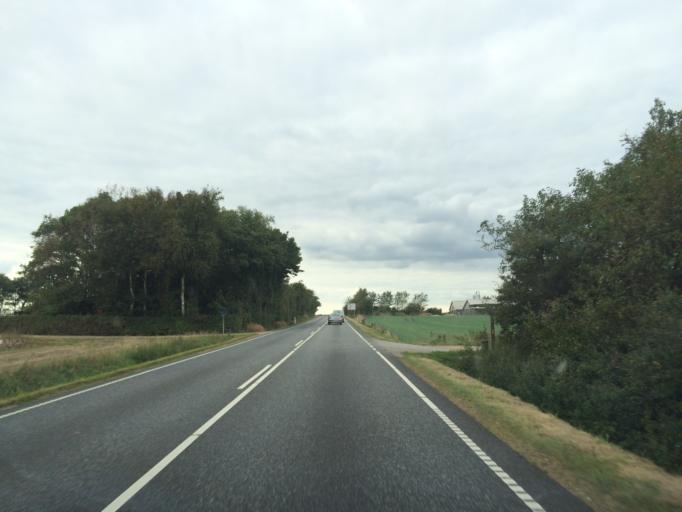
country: DK
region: Central Jutland
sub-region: Ringkobing-Skjern Kommune
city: Skjern
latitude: 56.0214
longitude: 8.4238
